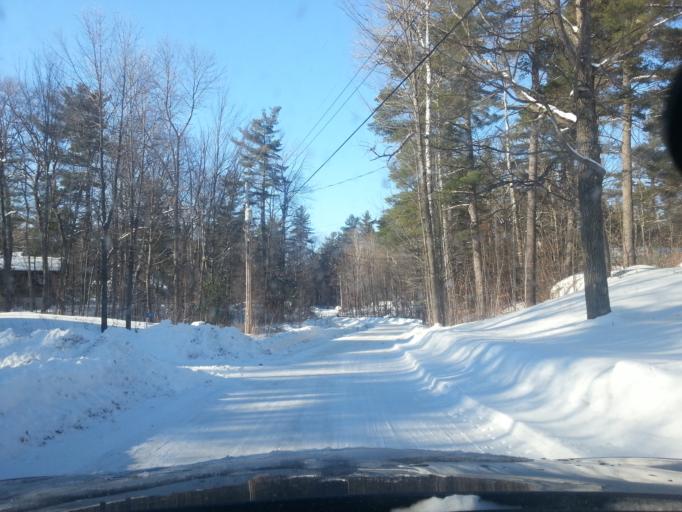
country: CA
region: Ontario
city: Arnprior
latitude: 45.3260
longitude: -76.3278
